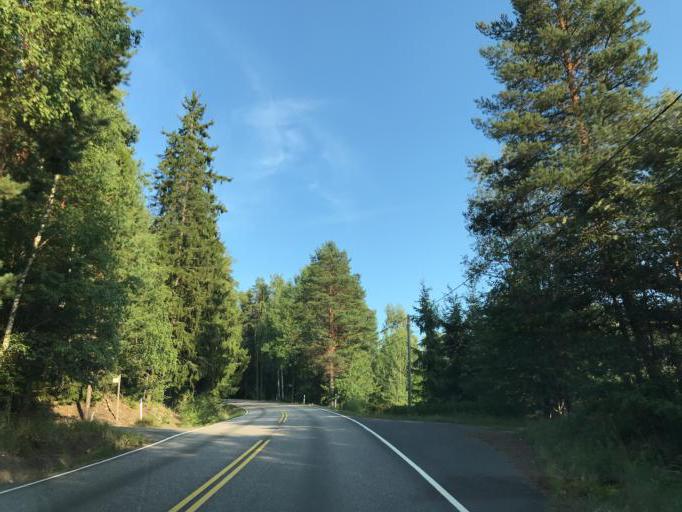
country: FI
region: Uusimaa
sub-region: Helsinki
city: Vihti
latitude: 60.4170
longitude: 24.4112
